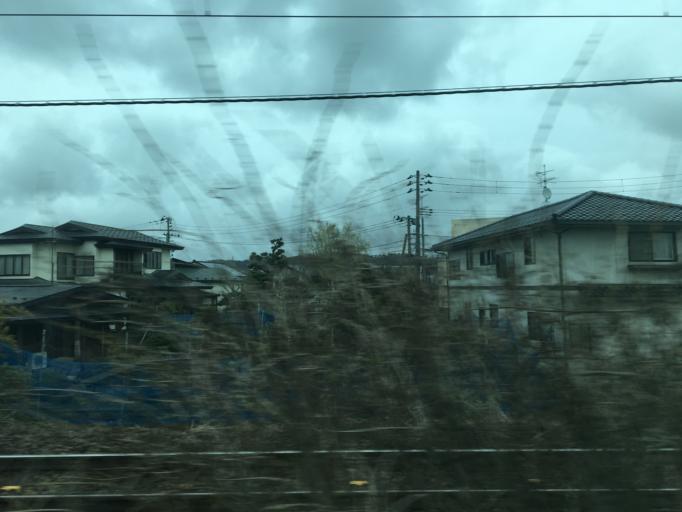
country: JP
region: Akita
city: Akita
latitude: 39.7307
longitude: 140.1257
